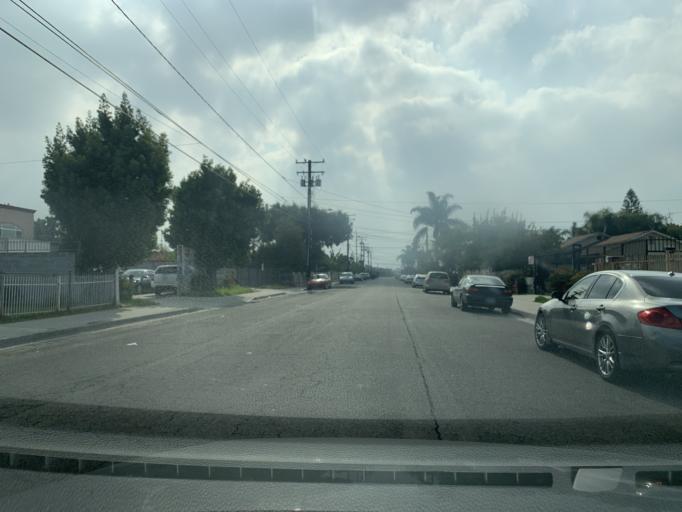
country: US
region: California
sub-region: Los Angeles County
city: South El Monte
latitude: 34.0544
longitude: -118.0541
